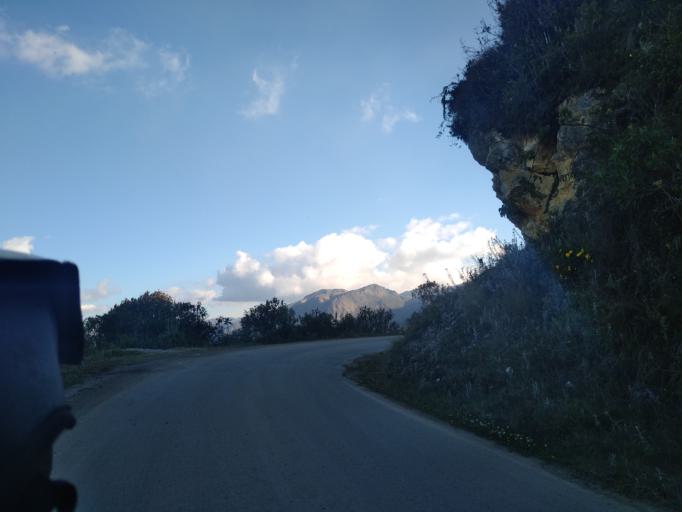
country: PE
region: Amazonas
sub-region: Provincia de Chachapoyas
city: Montevideo
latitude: -6.7192
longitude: -77.8648
